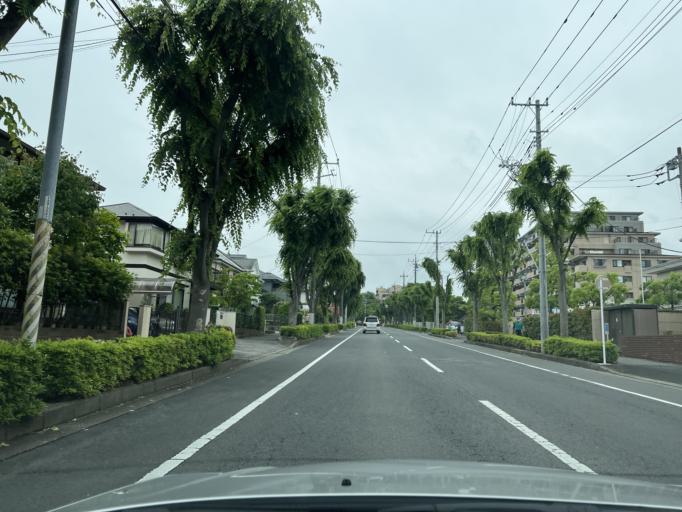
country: JP
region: Chiba
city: Nagareyama
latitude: 35.8615
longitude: 139.9045
